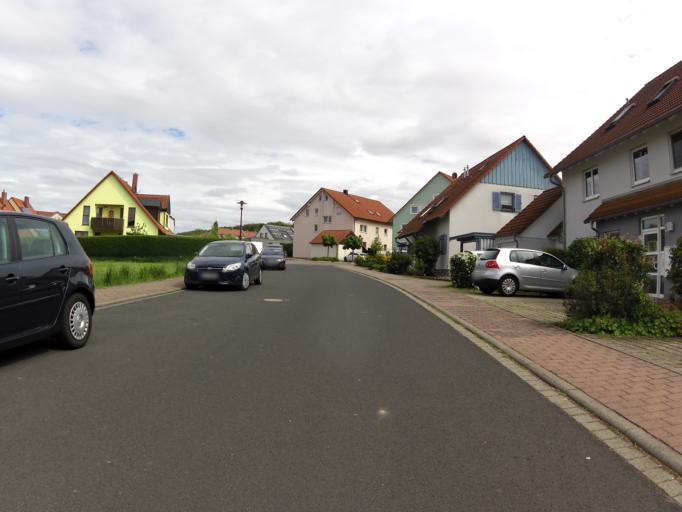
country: DE
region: Bavaria
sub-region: Regierungsbezirk Unterfranken
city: Kurnach
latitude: 49.8407
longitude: 10.0441
